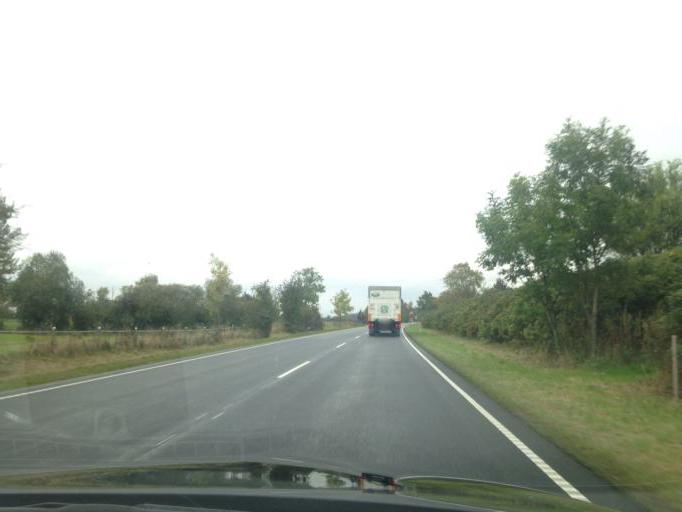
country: DK
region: South Denmark
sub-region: Kolding Kommune
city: Christiansfeld
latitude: 55.3602
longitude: 9.4788
